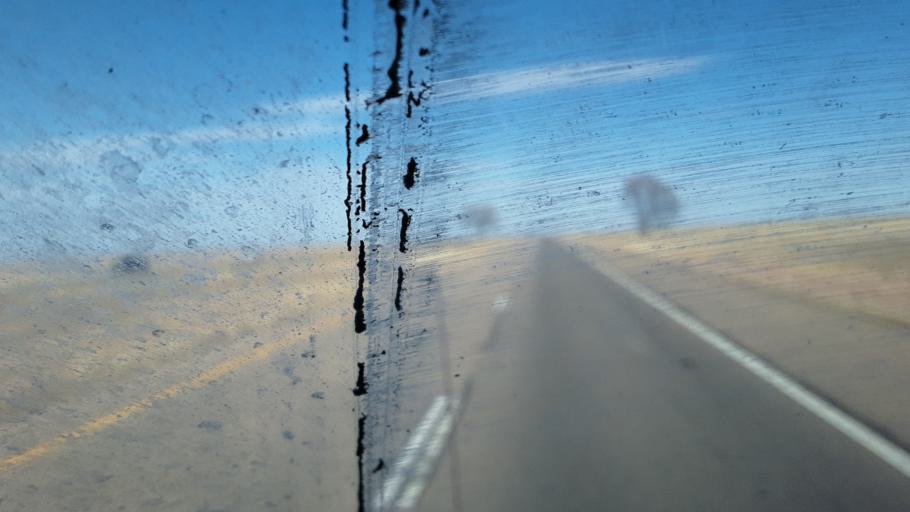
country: US
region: Colorado
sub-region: Weld County
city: Keenesburg
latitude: 40.1345
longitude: -104.4848
